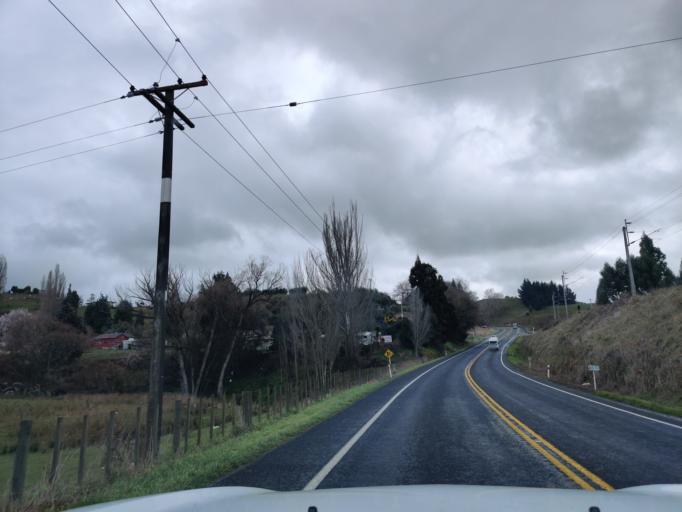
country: NZ
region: Manawatu-Wanganui
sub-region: Ruapehu District
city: Waiouru
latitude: -39.6890
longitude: 175.8082
